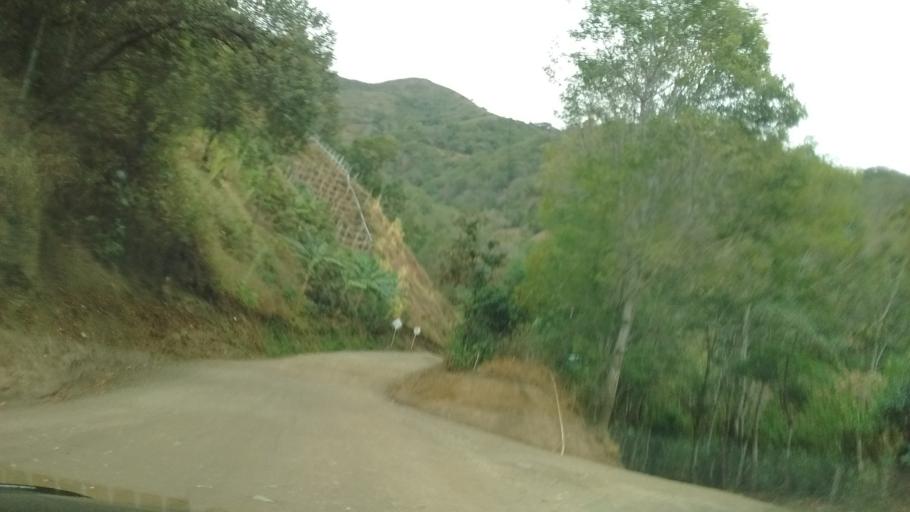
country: CO
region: Cauca
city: Almaguer
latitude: 1.8459
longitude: -76.9224
